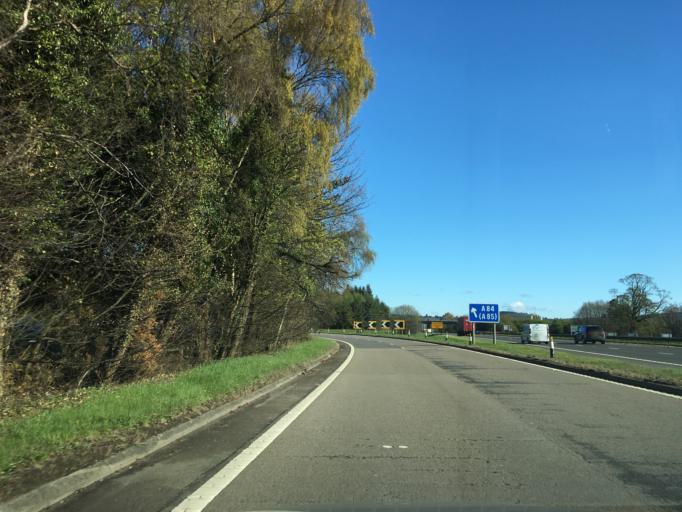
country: GB
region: Scotland
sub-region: Stirling
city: Bridge of Allan
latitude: 56.1311
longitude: -3.9709
